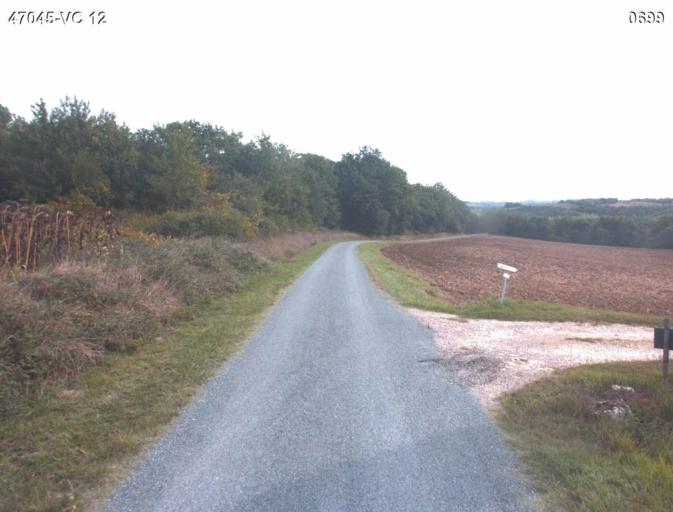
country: FR
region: Aquitaine
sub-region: Departement du Lot-et-Garonne
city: Nerac
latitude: 44.1437
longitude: 0.4242
